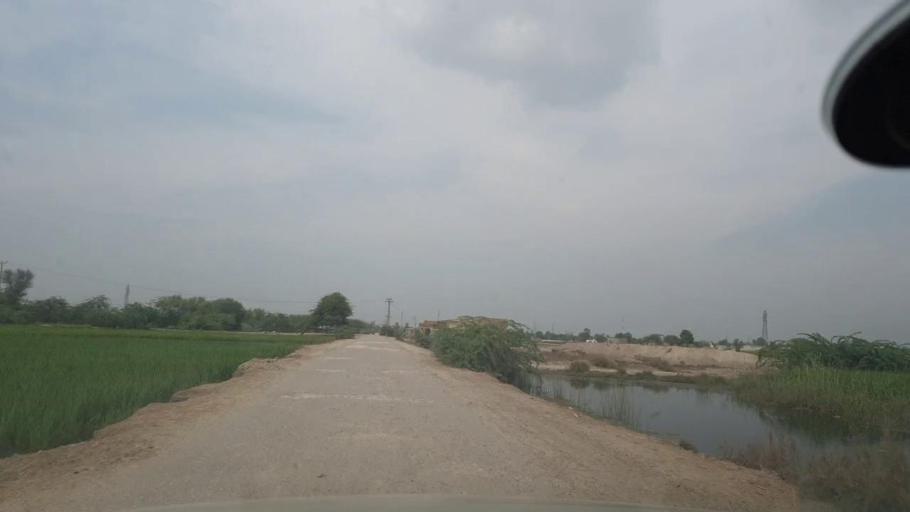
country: PK
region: Sindh
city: Jacobabad
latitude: 28.2581
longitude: 68.4373
